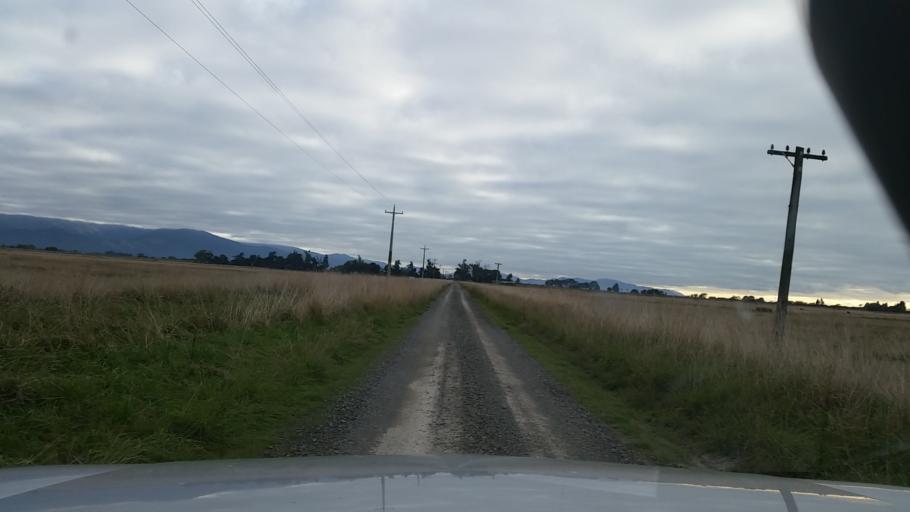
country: NZ
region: Marlborough
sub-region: Marlborough District
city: Blenheim
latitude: -41.5075
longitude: 174.0300
